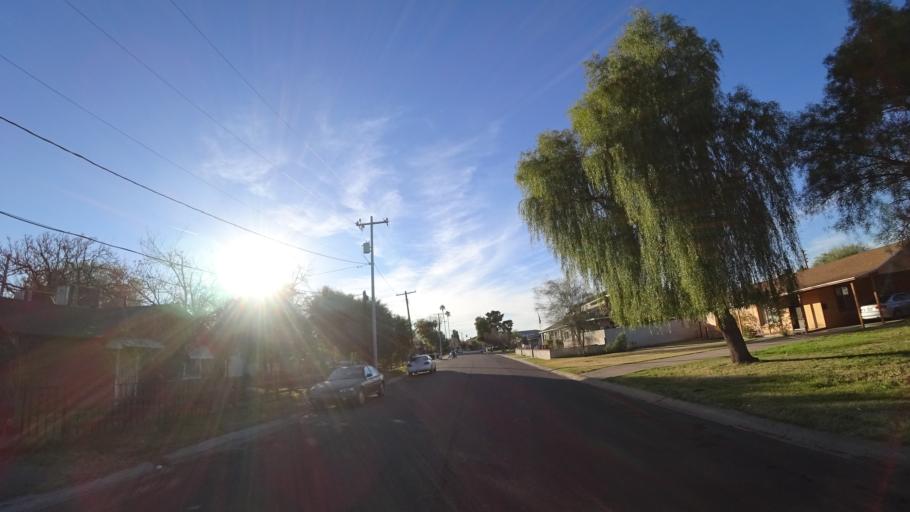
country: US
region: Arizona
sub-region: Maricopa County
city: Phoenix
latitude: 33.4769
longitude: -112.1056
